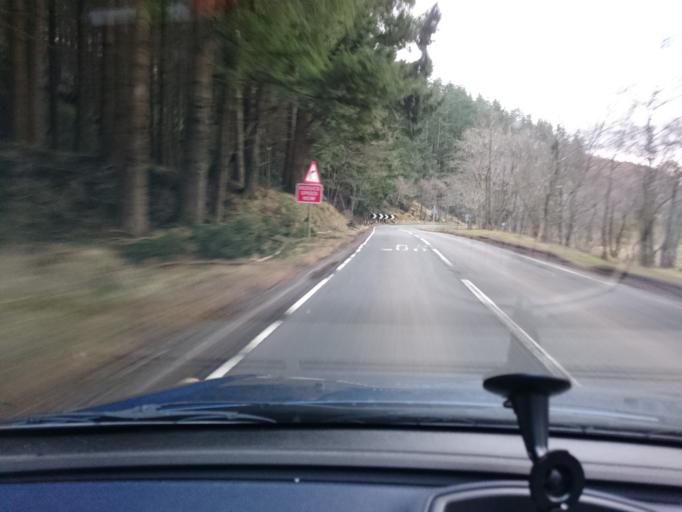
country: GB
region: Scotland
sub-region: Stirling
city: Callander
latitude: 56.2772
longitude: -4.2827
